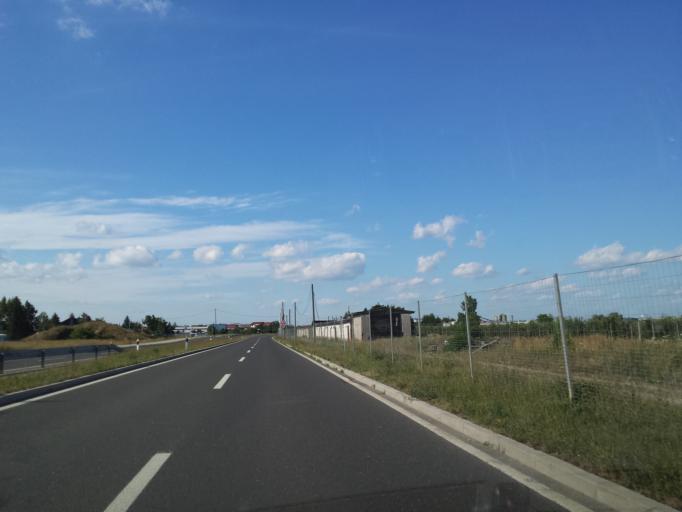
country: HR
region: Zagrebacka
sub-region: Grad Velika Gorica
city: Velika Gorica
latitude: 45.7037
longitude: 16.0816
